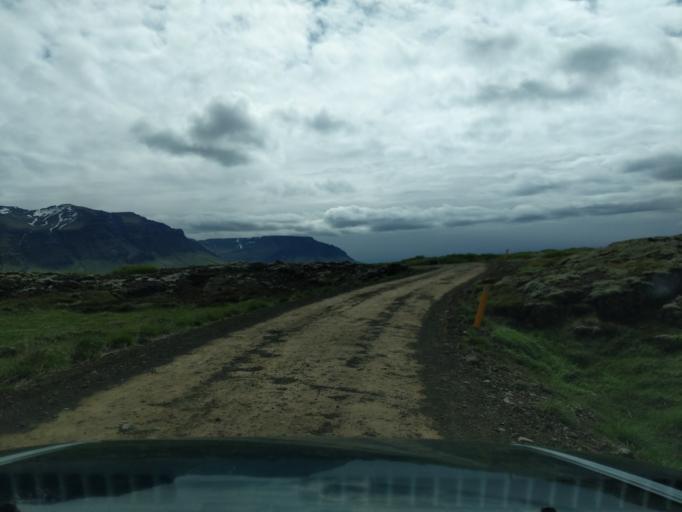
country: IS
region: West
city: Stykkisholmur
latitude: 64.8340
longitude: -22.3073
